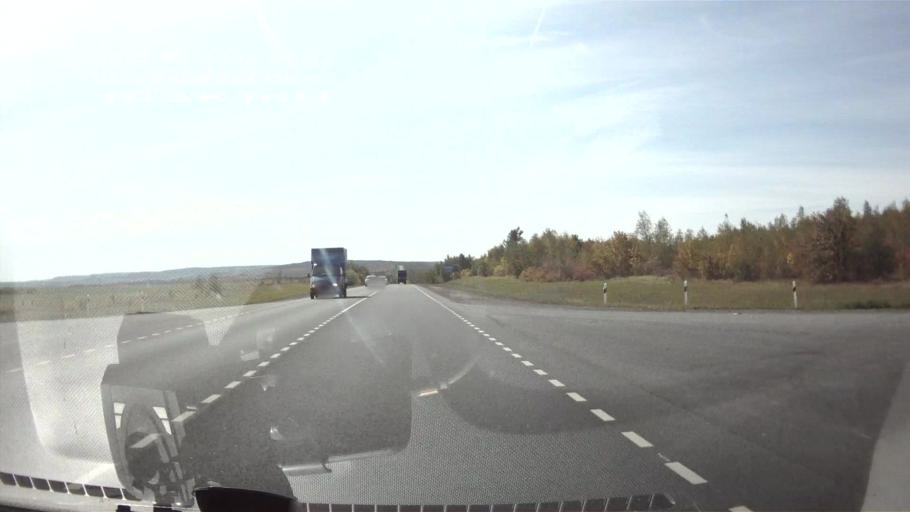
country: RU
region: Saratov
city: Khvalynsk
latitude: 52.5879
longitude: 48.1263
